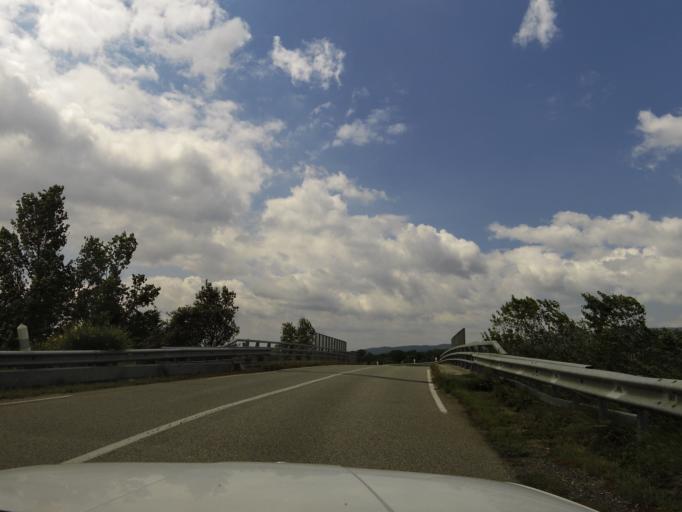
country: FR
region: Rhone-Alpes
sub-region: Departement de la Drome
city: Savasse
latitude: 44.6031
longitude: 4.7531
